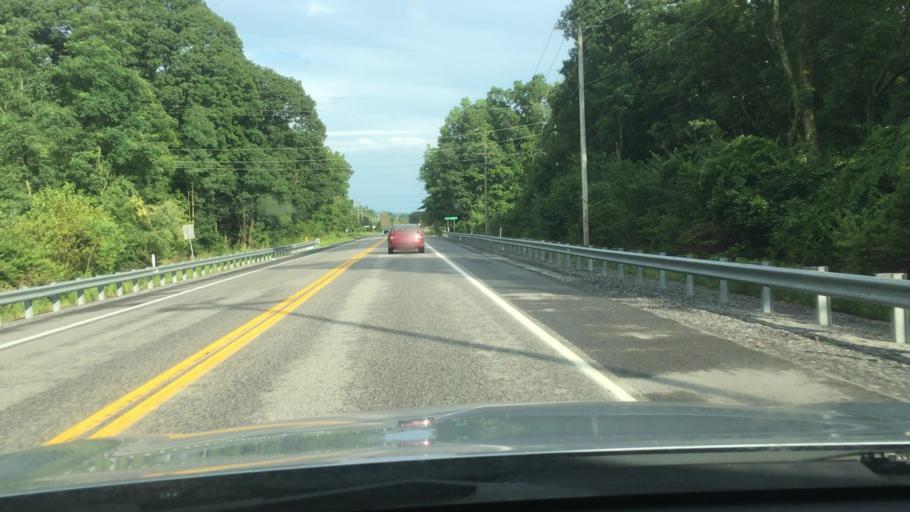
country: US
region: Pennsylvania
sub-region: York County
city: Dillsburg
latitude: 40.0922
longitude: -76.9543
